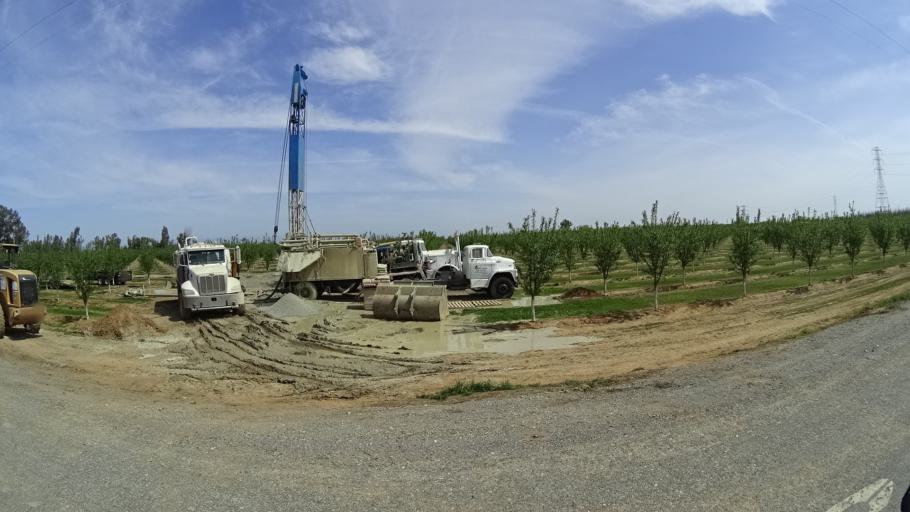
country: US
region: California
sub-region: Glenn County
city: Orland
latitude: 39.7881
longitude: -122.1503
